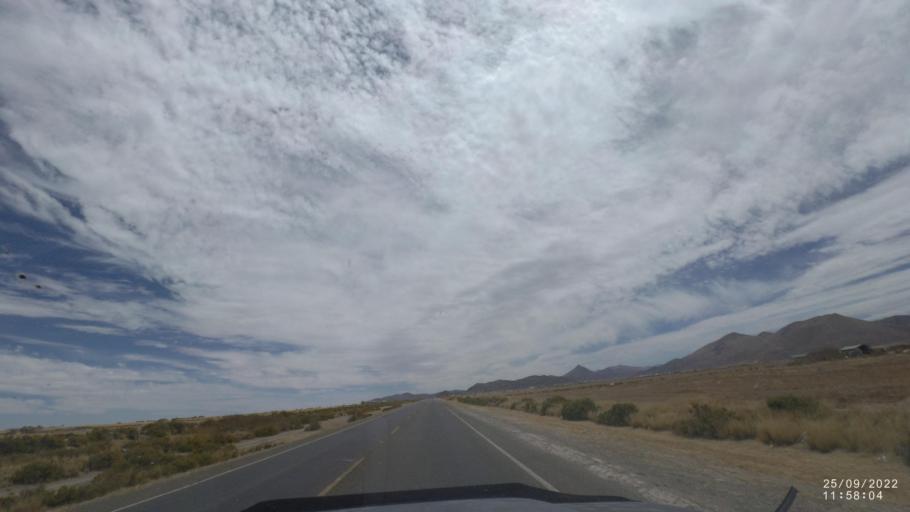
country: BO
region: Oruro
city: Challapata
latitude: -18.8113
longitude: -66.8339
